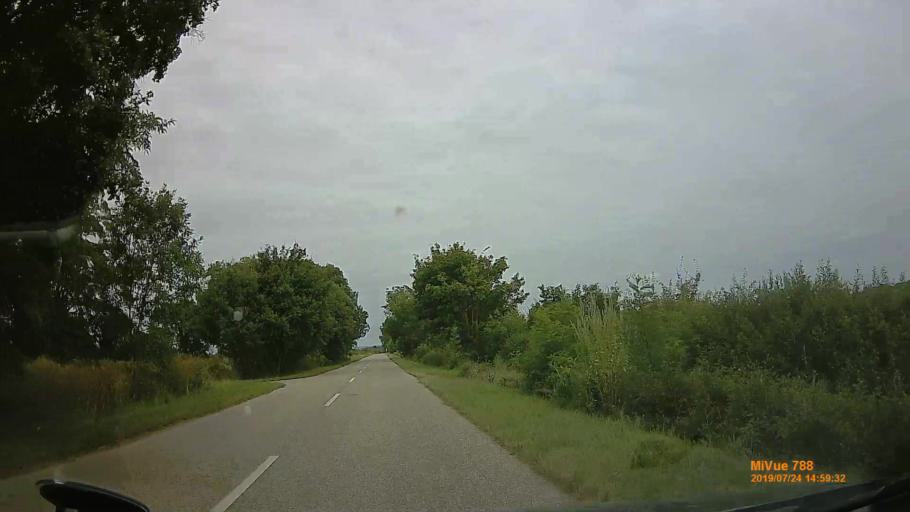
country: HU
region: Szabolcs-Szatmar-Bereg
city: Aranyosapati
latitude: 48.2301
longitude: 22.3505
